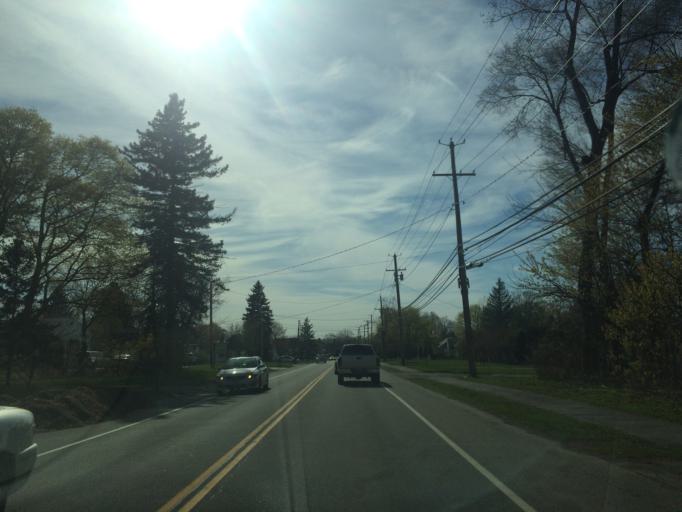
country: US
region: New York
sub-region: Monroe County
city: Fairport
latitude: 43.1086
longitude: -77.4554
